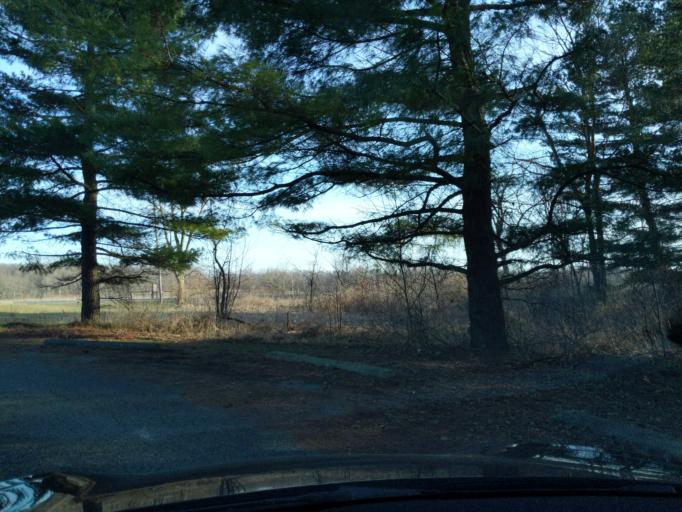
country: US
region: Michigan
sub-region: Ionia County
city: Ionia
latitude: 42.9560
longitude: -85.1295
